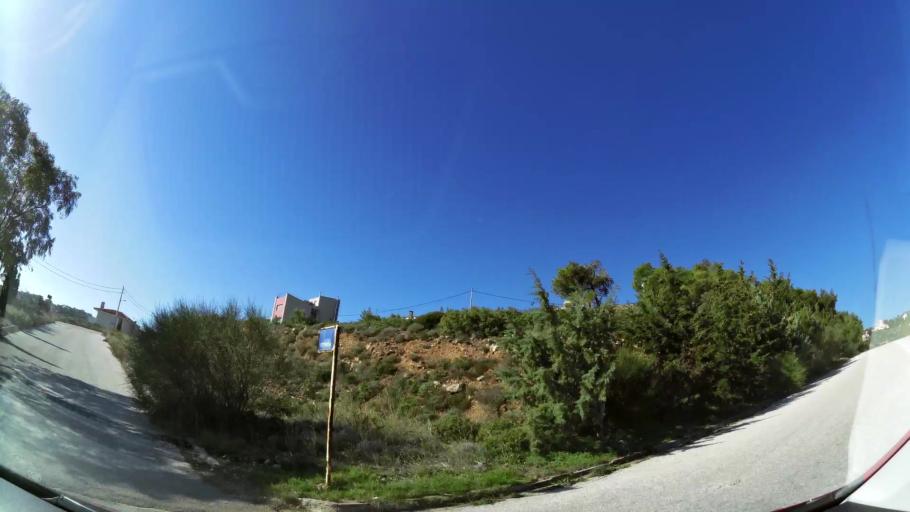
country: GR
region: Attica
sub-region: Nomarchia Anatolikis Attikis
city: Dhrafi
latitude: 38.0337
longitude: 23.9020
